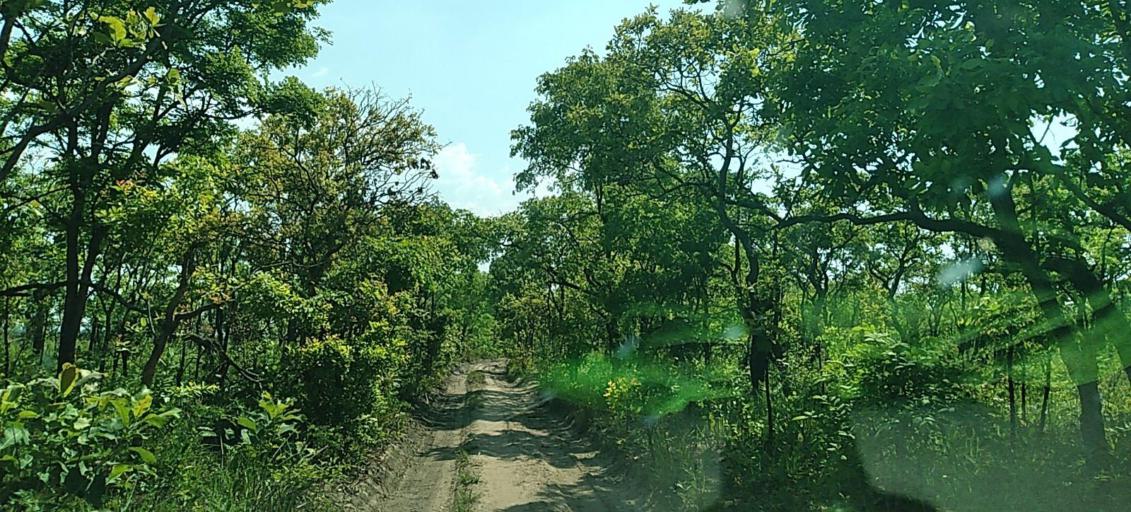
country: CD
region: Katanga
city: Kolwezi
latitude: -11.2611
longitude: 25.0078
